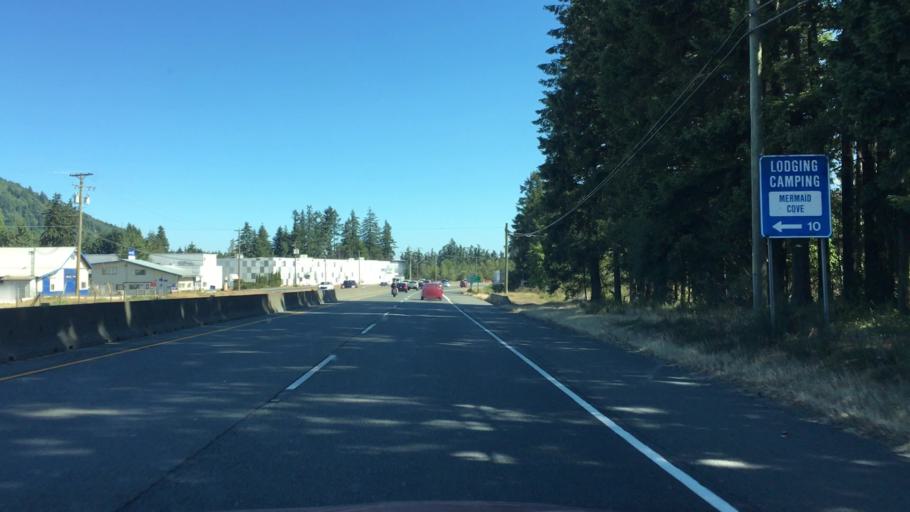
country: CA
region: British Columbia
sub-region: Cowichan Valley Regional District
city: Ladysmith
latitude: 49.0391
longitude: -123.8661
